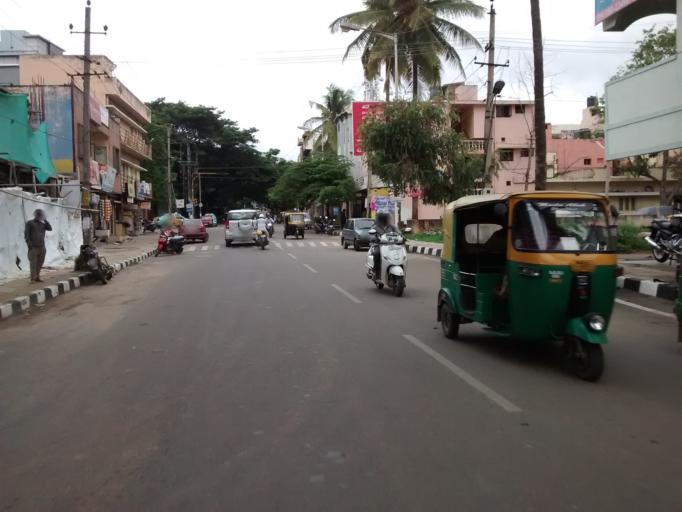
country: IN
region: Karnataka
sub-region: Bangalore Urban
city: Yelahanka
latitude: 13.0423
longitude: 77.5823
